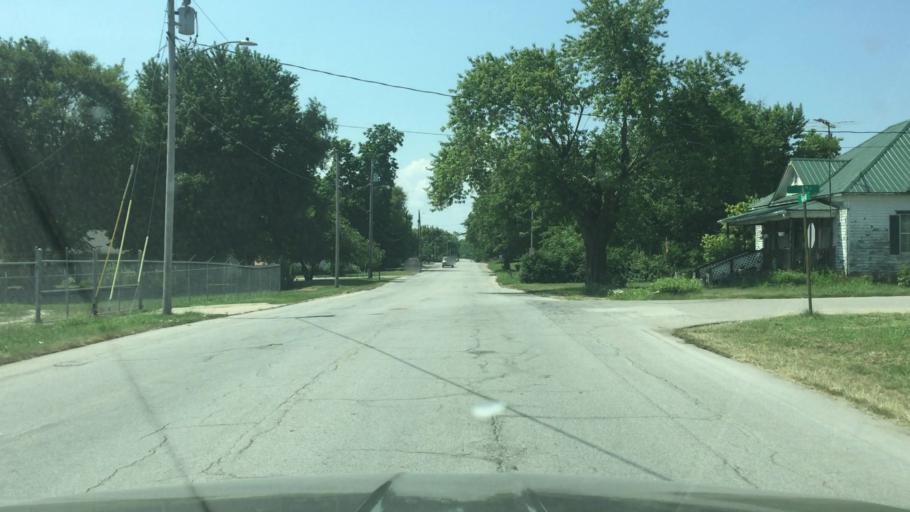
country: US
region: Missouri
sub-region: Miller County
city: Eldon
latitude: 38.3457
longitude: -92.5864
